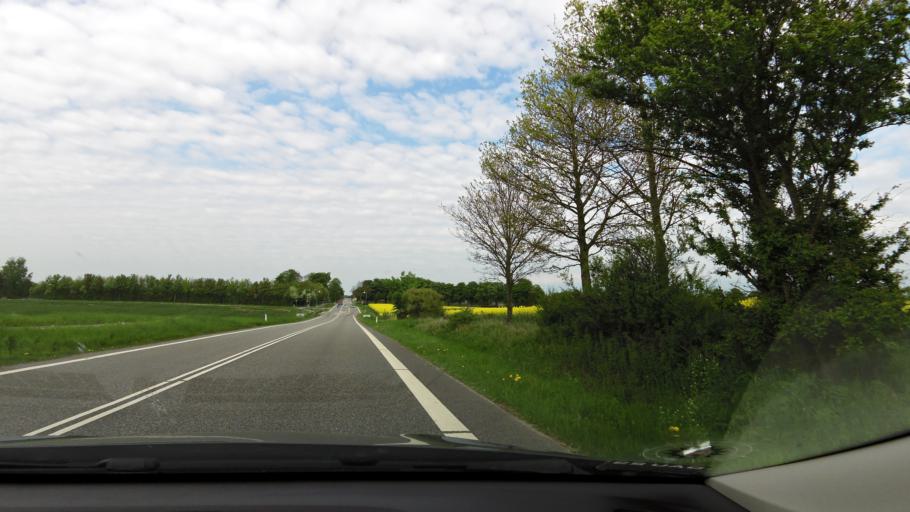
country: DK
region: South Denmark
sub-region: Nyborg Kommune
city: Ullerslev
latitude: 55.2772
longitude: 10.6841
